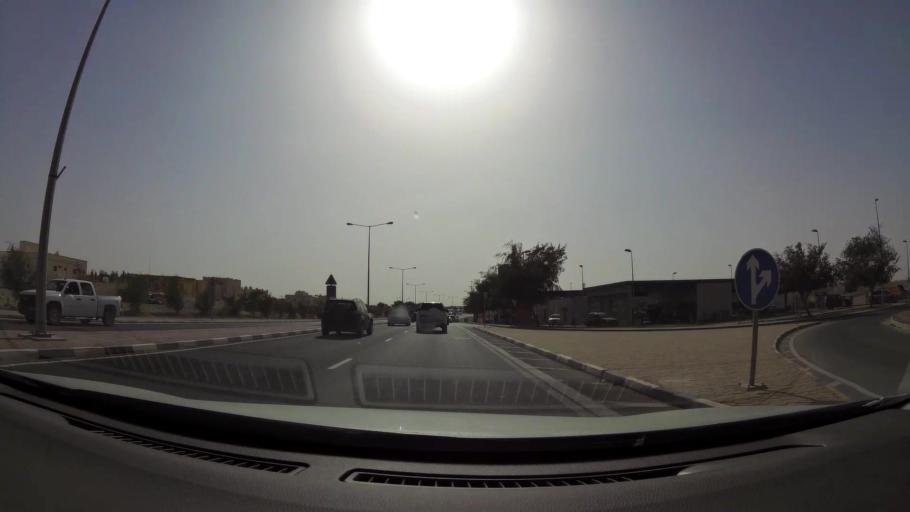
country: QA
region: Baladiyat ar Rayyan
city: Ar Rayyan
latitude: 25.3417
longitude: 51.4360
